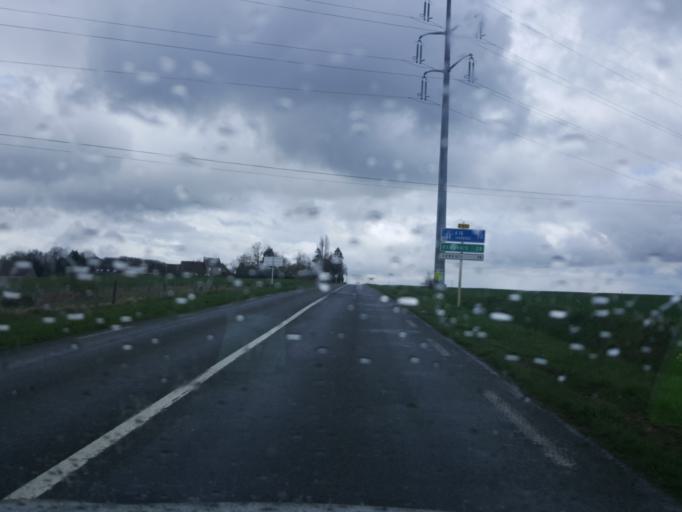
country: FR
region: Picardie
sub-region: Departement de l'Oise
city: Trie-Chateau
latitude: 49.2830
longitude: 1.8361
